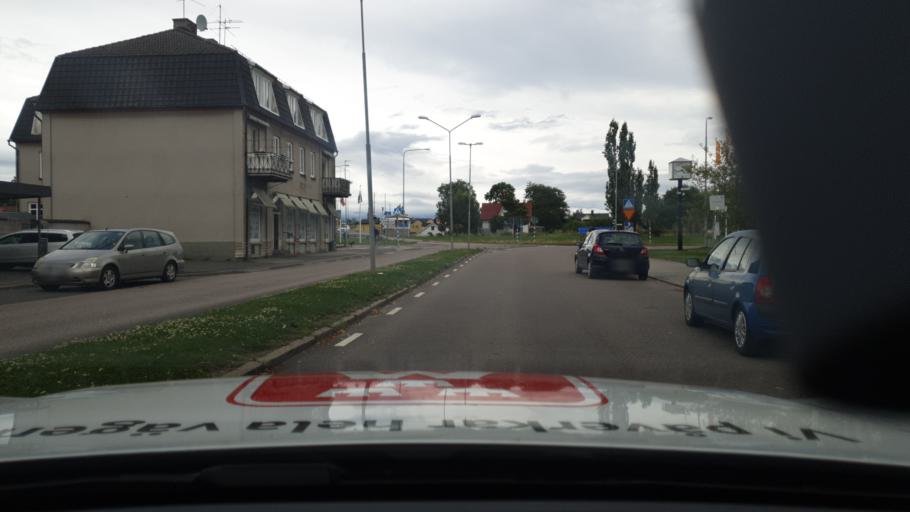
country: SE
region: Vaestra Goetaland
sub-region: Toreboda Kommun
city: Toereboda
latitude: 58.7097
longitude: 14.1268
